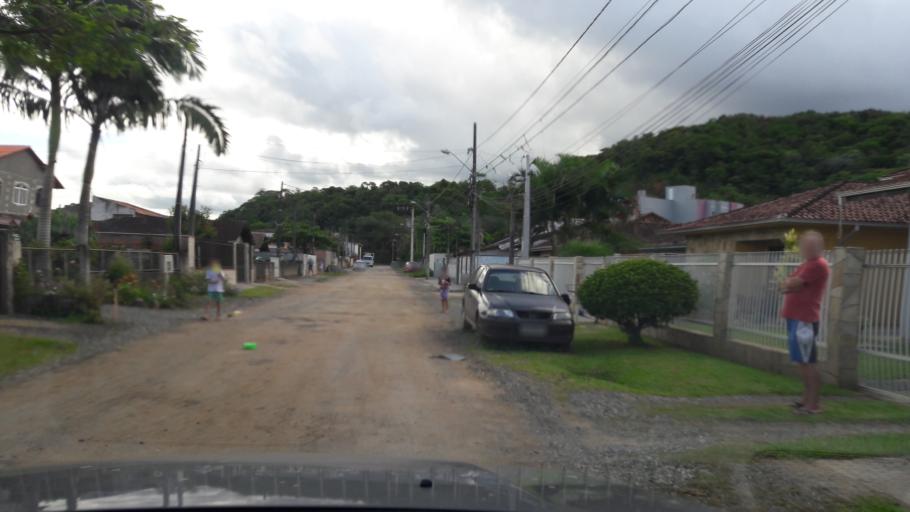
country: BR
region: Santa Catarina
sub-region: Joinville
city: Joinville
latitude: -26.3233
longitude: -48.8205
